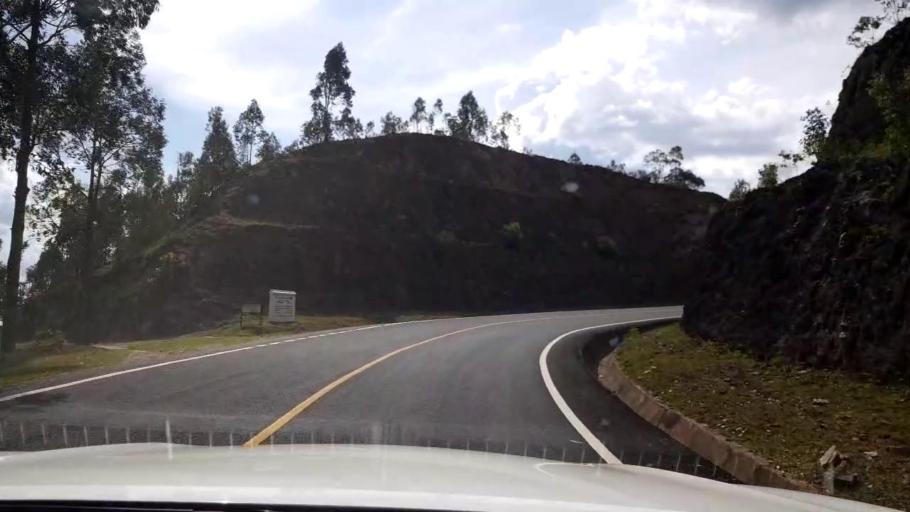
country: RW
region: Southern Province
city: Gitarama
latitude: -2.0317
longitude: 29.7173
